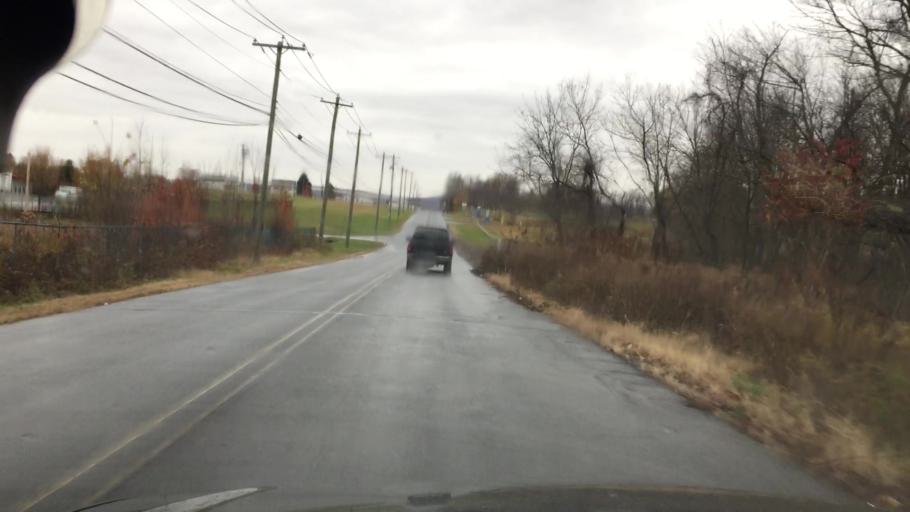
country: US
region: Pennsylvania
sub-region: Luzerne County
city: Nanticoke
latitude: 41.1893
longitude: -75.9943
